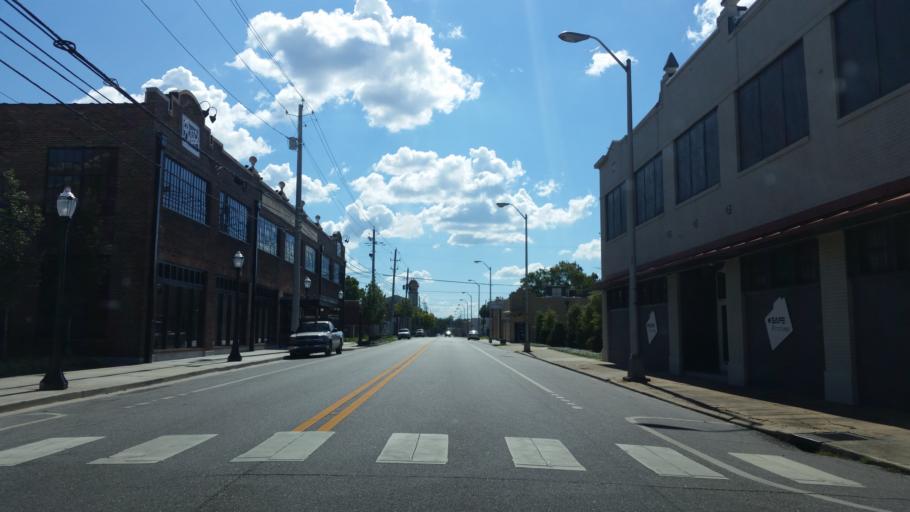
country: US
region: Alabama
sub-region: Mobile County
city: Mobile
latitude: 30.6926
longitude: -88.0483
